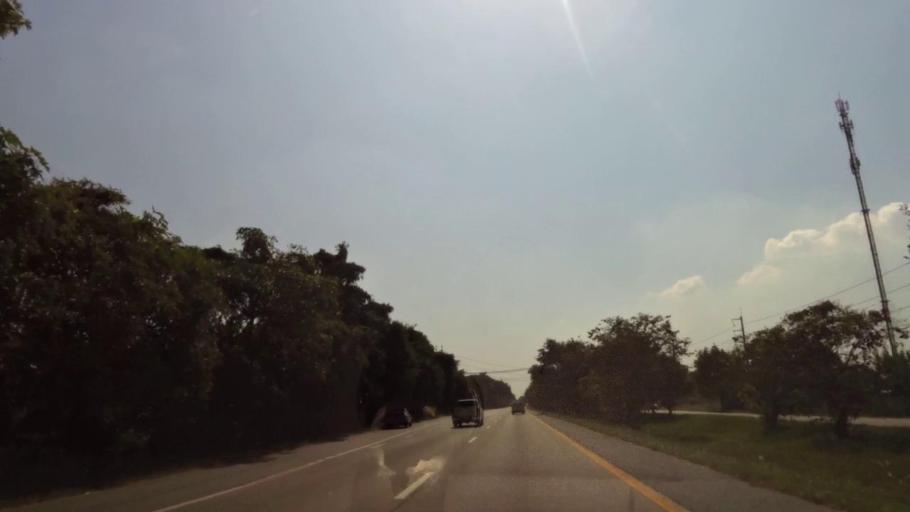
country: TH
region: Phichit
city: Wachira Barami
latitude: 16.5764
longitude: 100.1481
